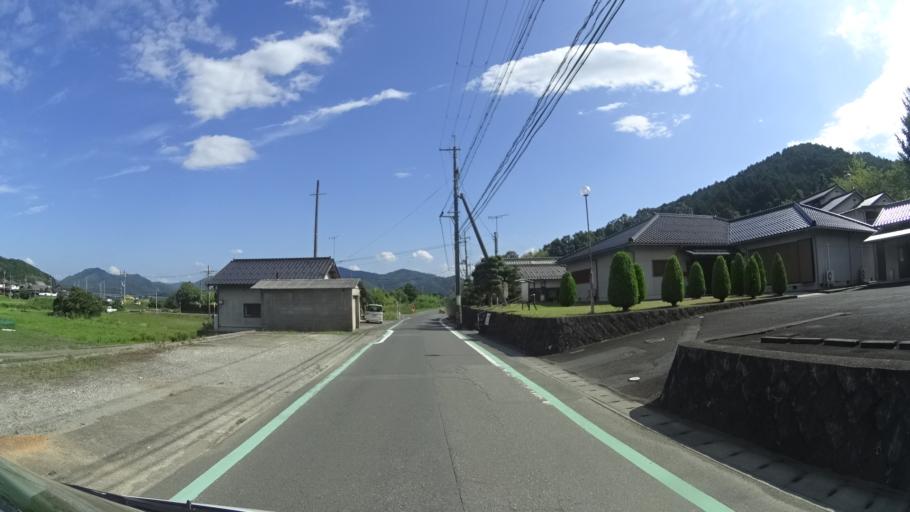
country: JP
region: Kyoto
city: Fukuchiyama
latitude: 35.3193
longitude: 135.1814
